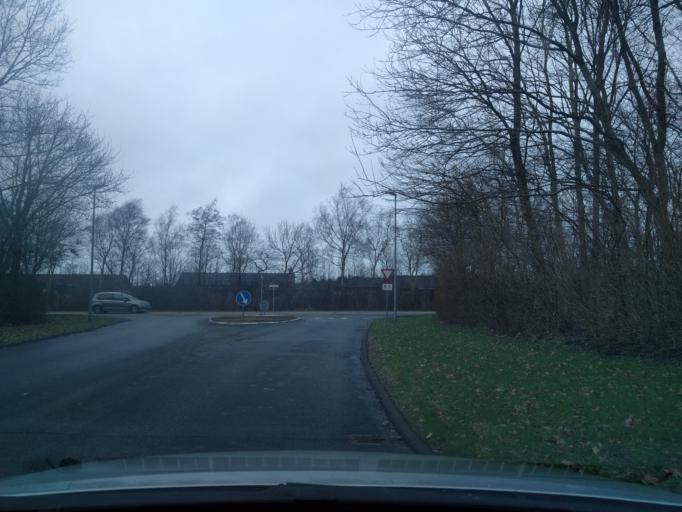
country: DK
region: South Denmark
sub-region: Tonder Kommune
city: Toftlund
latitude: 55.1833
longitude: 9.0765
